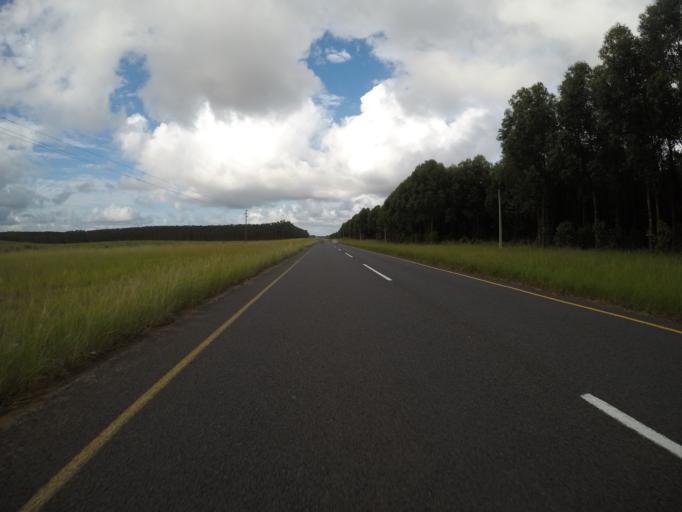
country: ZA
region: KwaZulu-Natal
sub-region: uMkhanyakude District Municipality
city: Mtubatuba
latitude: -28.3903
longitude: 32.2280
